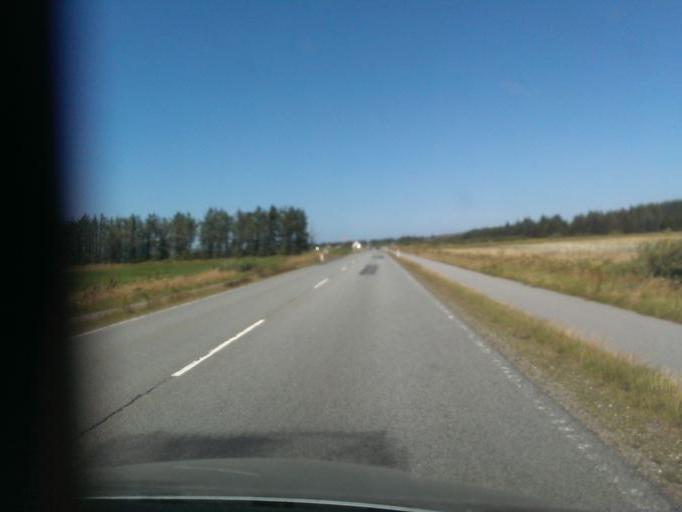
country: DK
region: North Denmark
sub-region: Jammerbugt Kommune
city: Pandrup
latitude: 57.3478
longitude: 9.7074
